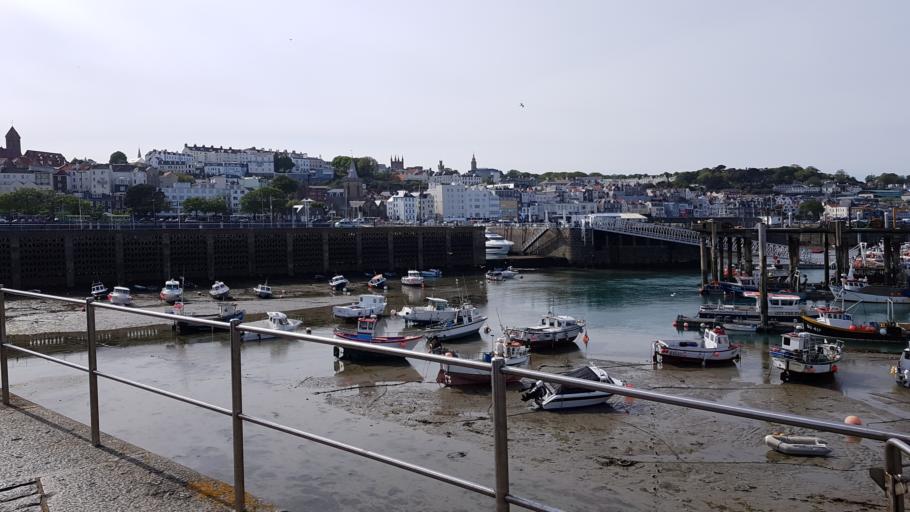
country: GG
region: St Peter Port
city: Saint Peter Port
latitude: 49.4531
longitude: -2.5316
